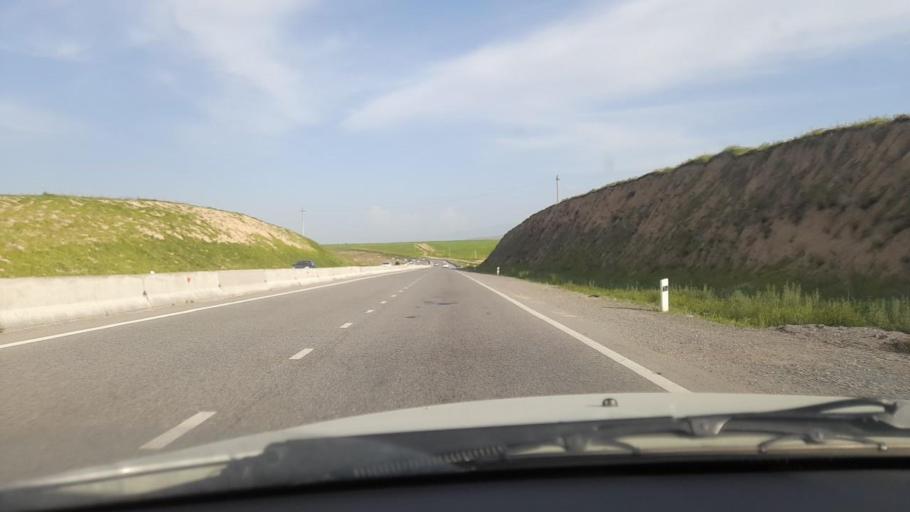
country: UZ
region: Jizzax
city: Jizzax
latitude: 40.0497
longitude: 67.7350
